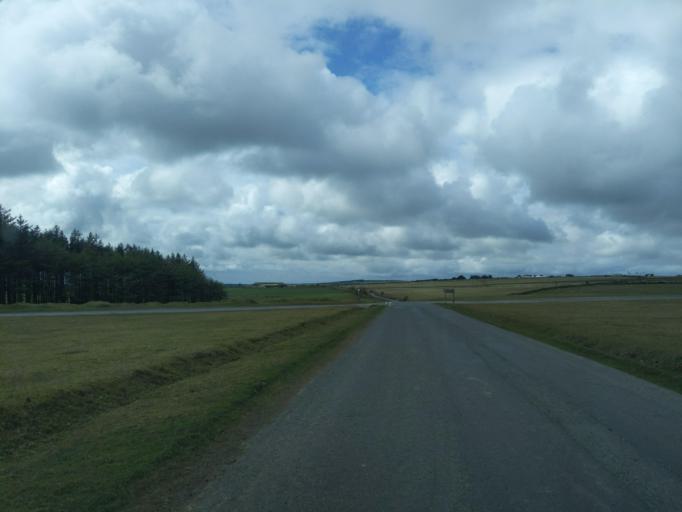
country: GB
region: England
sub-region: Cornwall
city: Camelford
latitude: 50.6395
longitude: -4.6291
